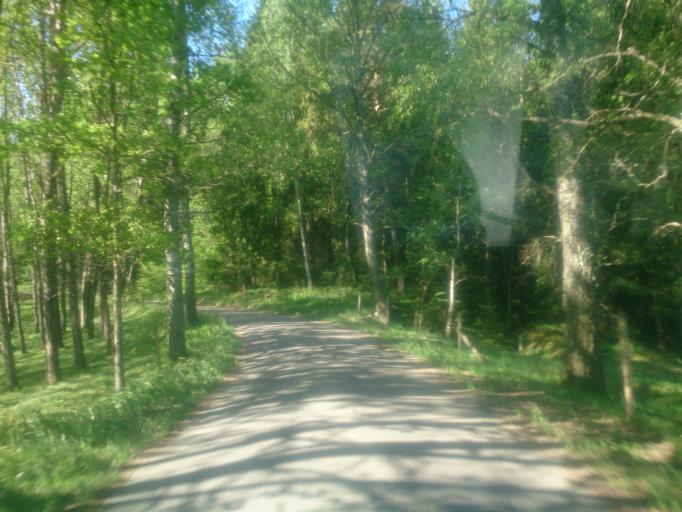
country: SE
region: OEstergoetland
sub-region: Atvidabergs Kommun
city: Atvidaberg
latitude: 58.3019
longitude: 16.0776
